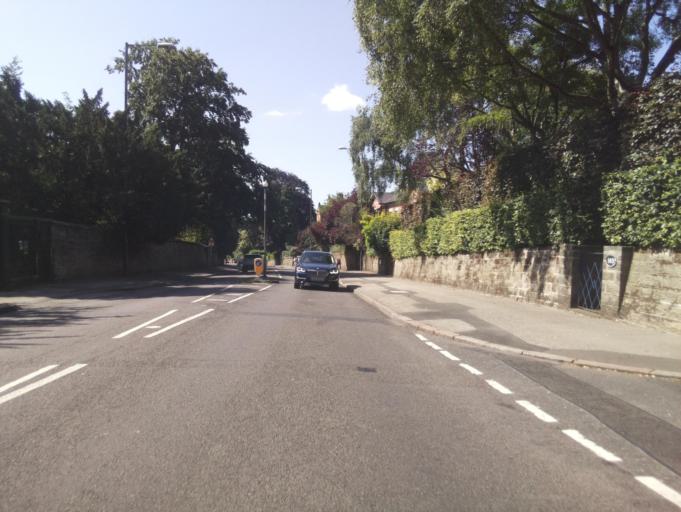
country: GB
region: England
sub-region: Derby
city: Derby
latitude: 52.9352
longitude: -1.4839
